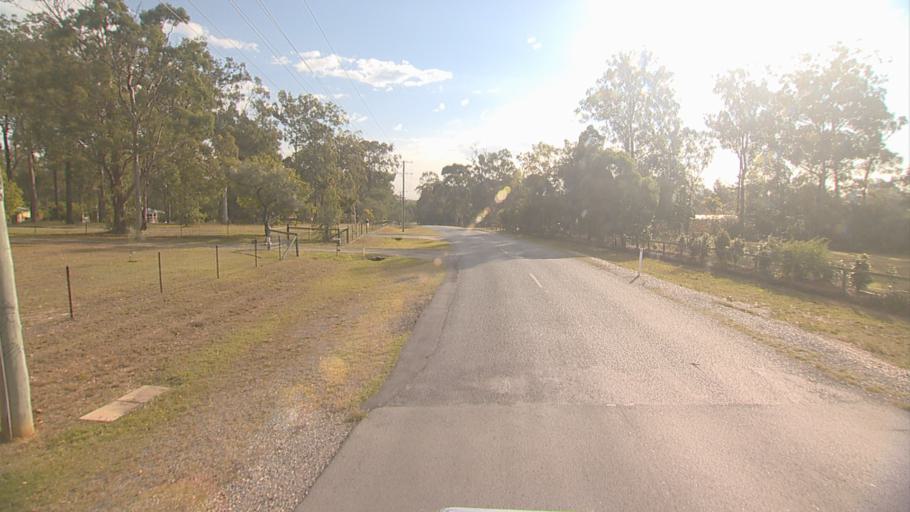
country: AU
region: Queensland
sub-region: Logan
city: Chambers Flat
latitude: -27.7789
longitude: 153.1080
